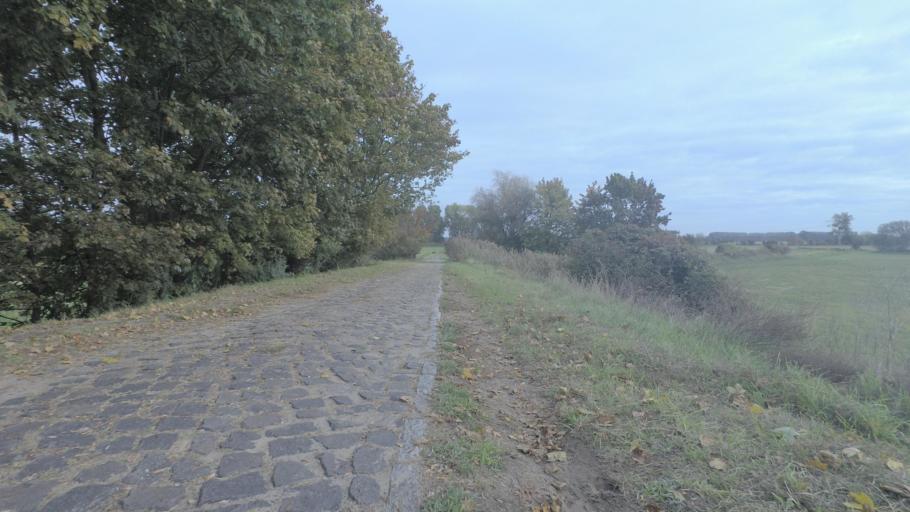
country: DE
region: Brandenburg
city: Grossbeeren
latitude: 52.3053
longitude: 13.3308
